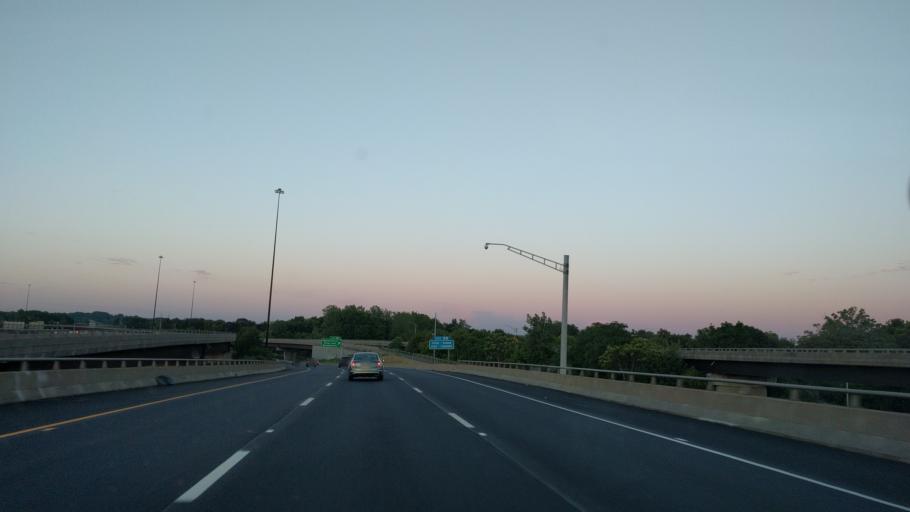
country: US
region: Connecticut
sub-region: Hartford County
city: East Hartford
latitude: 41.7632
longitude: -72.6349
